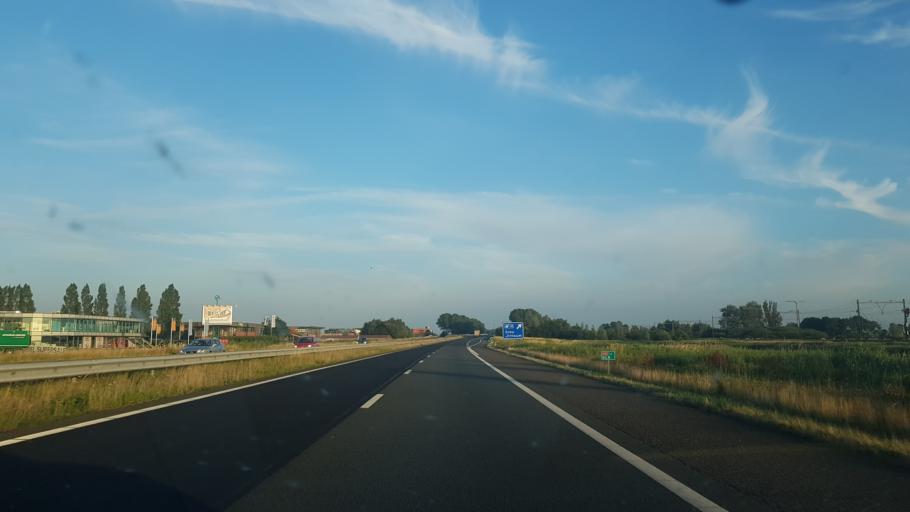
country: NL
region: Friesland
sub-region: Gemeente Boarnsterhim
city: Grou
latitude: 53.0973
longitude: 5.8200
